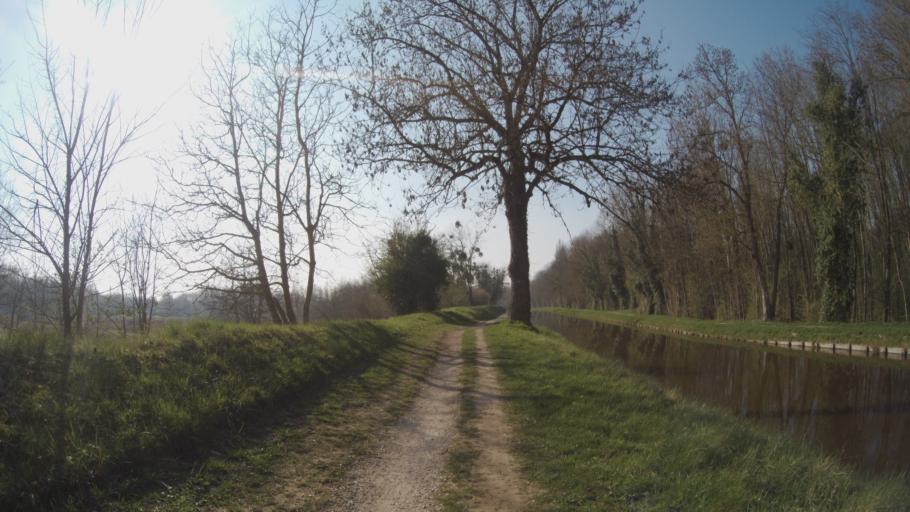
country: FR
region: Centre
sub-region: Departement du Loiret
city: Checy
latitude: 47.8927
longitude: 2.0134
